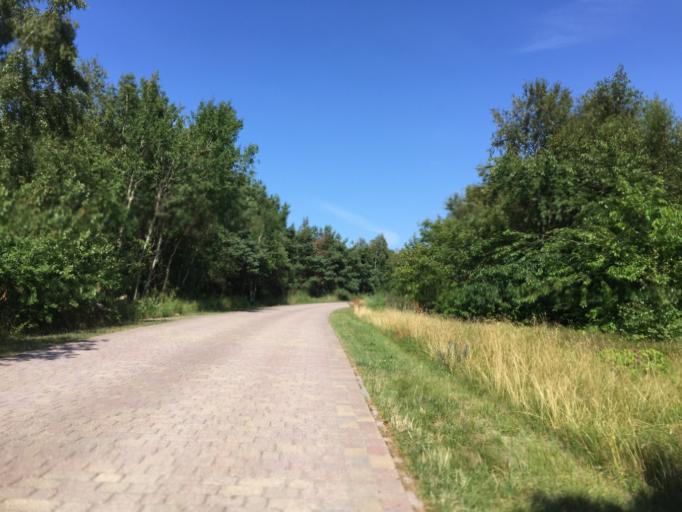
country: DE
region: Mecklenburg-Vorpommern
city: Hiddensee
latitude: 54.5345
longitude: 13.0897
